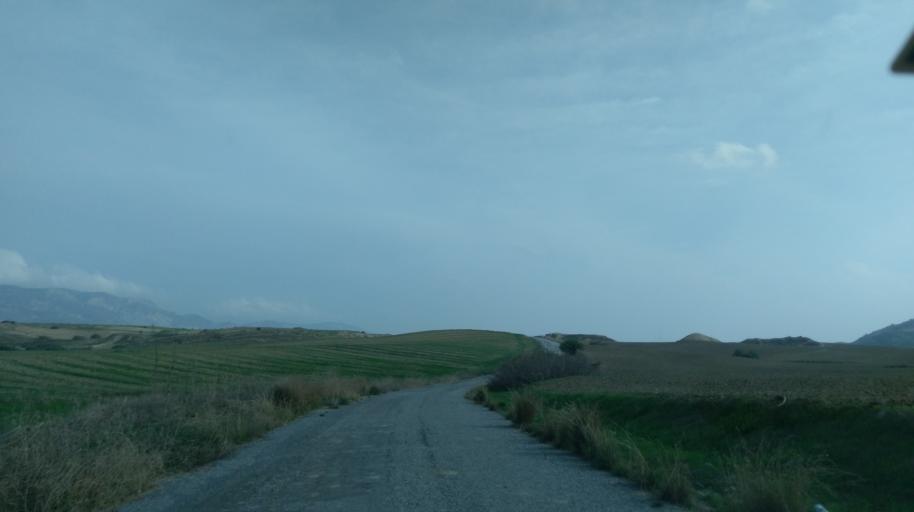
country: CY
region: Keryneia
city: Lapithos
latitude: 35.2621
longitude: 33.1003
